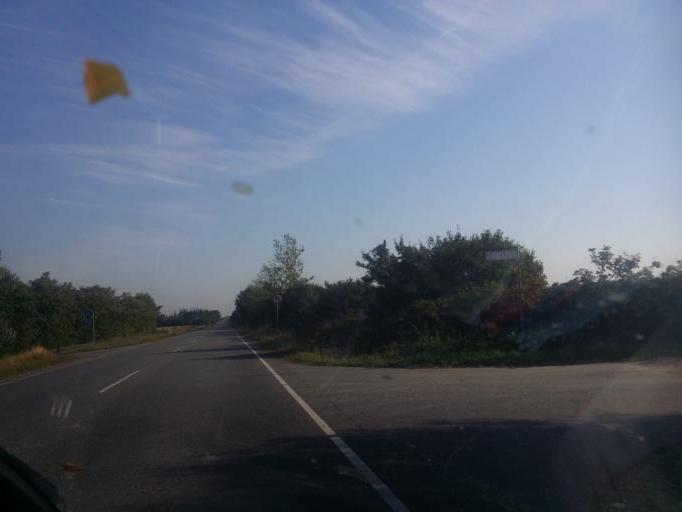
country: DK
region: South Denmark
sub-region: Esbjerg Kommune
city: Ribe
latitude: 55.3009
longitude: 8.7432
